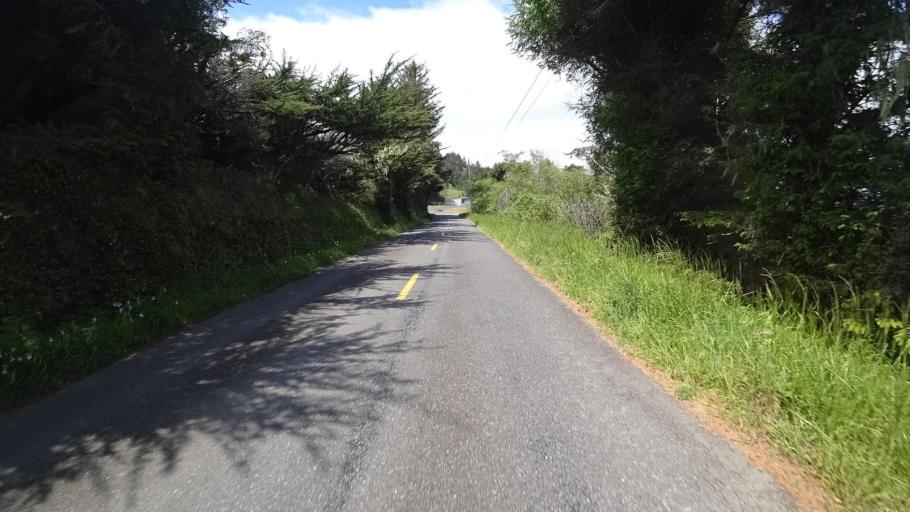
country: US
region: California
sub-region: Humboldt County
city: Humboldt Hill
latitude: 40.6748
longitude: -124.2209
